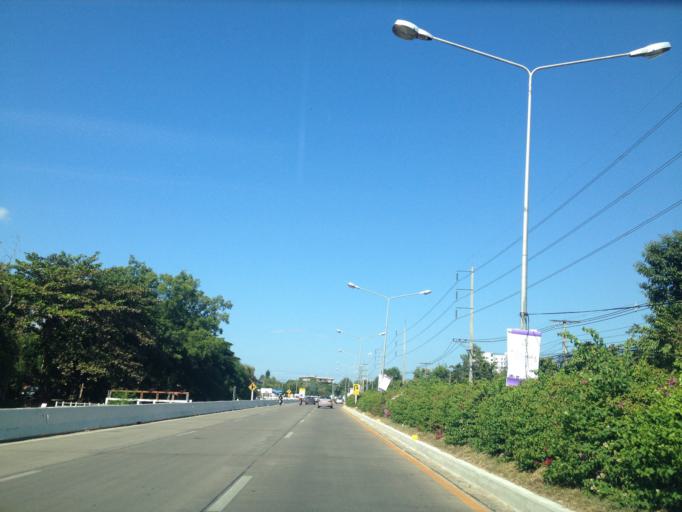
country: TH
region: Chiang Mai
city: Chiang Mai
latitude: 18.8142
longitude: 98.9633
